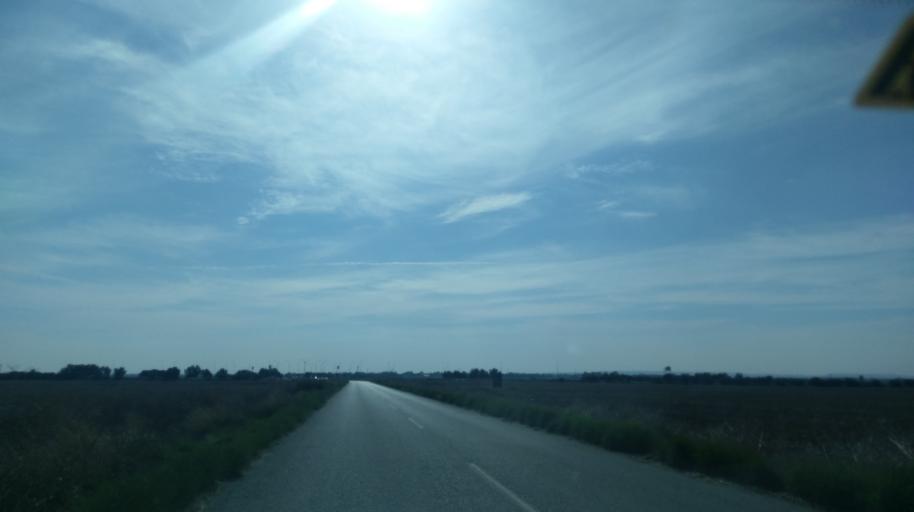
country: CY
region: Ammochostos
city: Lefkonoiko
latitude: 35.1869
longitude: 33.6998
